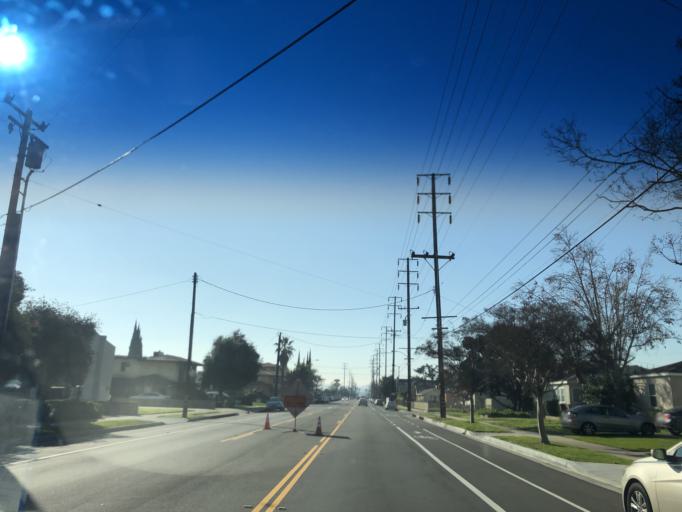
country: US
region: California
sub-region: Los Angeles County
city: East San Gabriel
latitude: 34.0833
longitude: -118.0996
